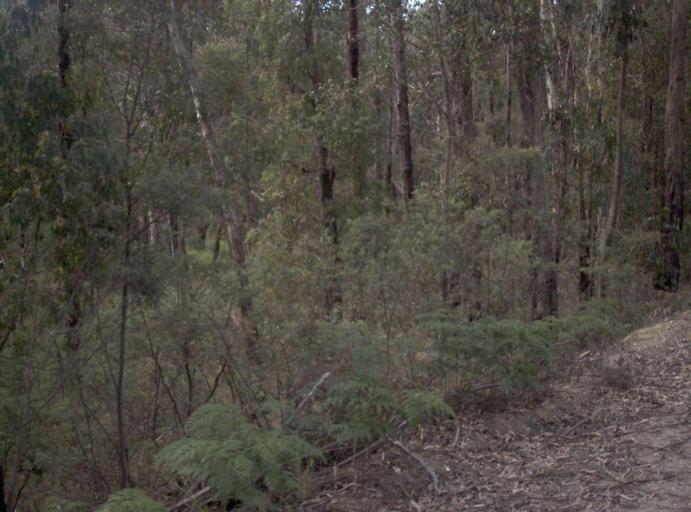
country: AU
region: New South Wales
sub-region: Bombala
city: Bombala
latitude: -37.1871
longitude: 148.7059
